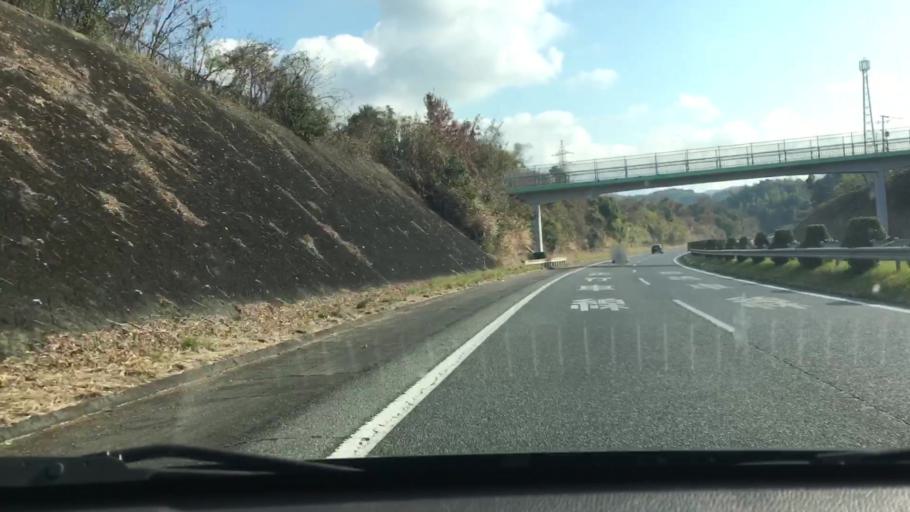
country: JP
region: Kumamoto
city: Matsubase
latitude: 32.6376
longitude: 130.7092
